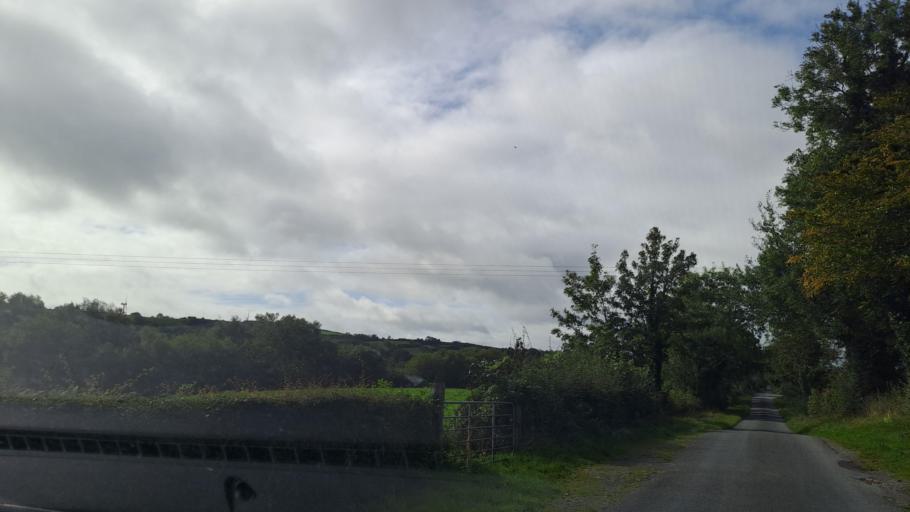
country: IE
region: Ulster
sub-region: An Cabhan
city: Bailieborough
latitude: 53.9722
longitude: -6.8845
